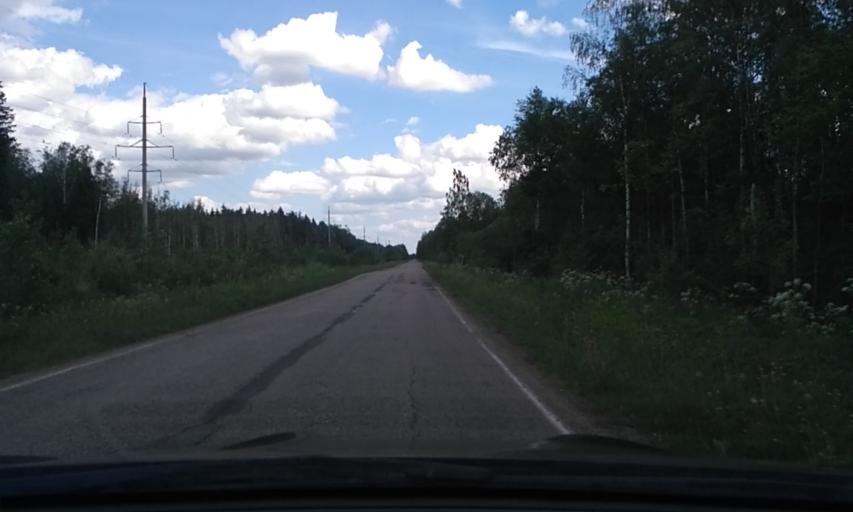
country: RU
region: Leningrad
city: Otradnoye
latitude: 59.8207
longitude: 30.7929
